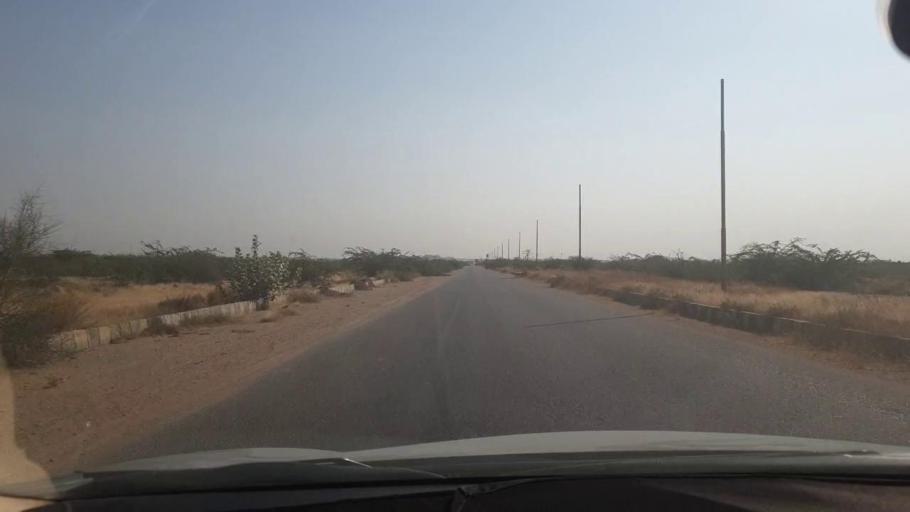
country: PK
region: Sindh
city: Malir Cantonment
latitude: 25.0655
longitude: 67.1390
